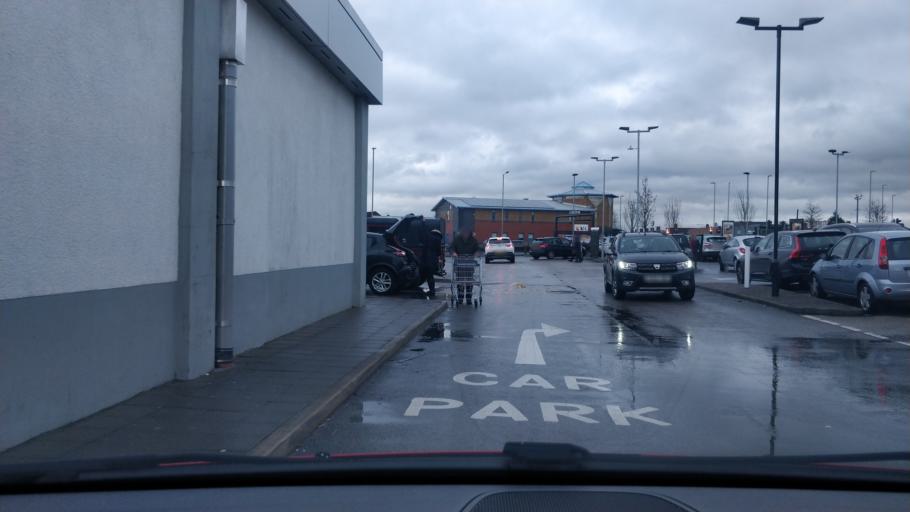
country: GB
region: England
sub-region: Knowsley
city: Huyton
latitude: 53.4221
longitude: -2.8624
